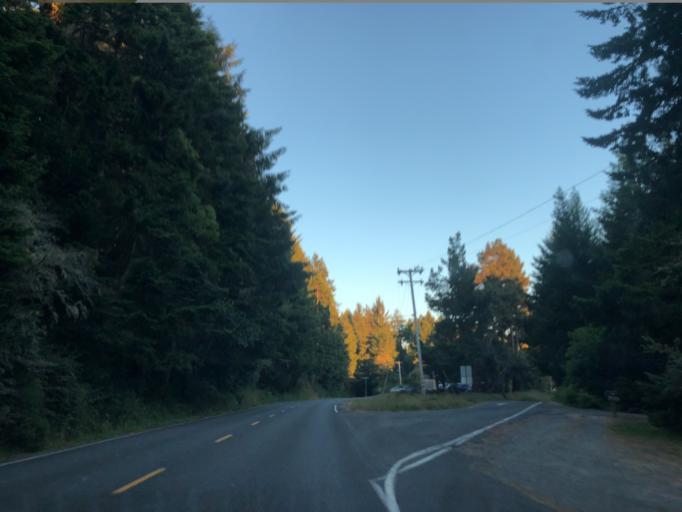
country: US
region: California
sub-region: Humboldt County
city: Westhaven-Moonstone
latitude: 41.0912
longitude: -124.1524
